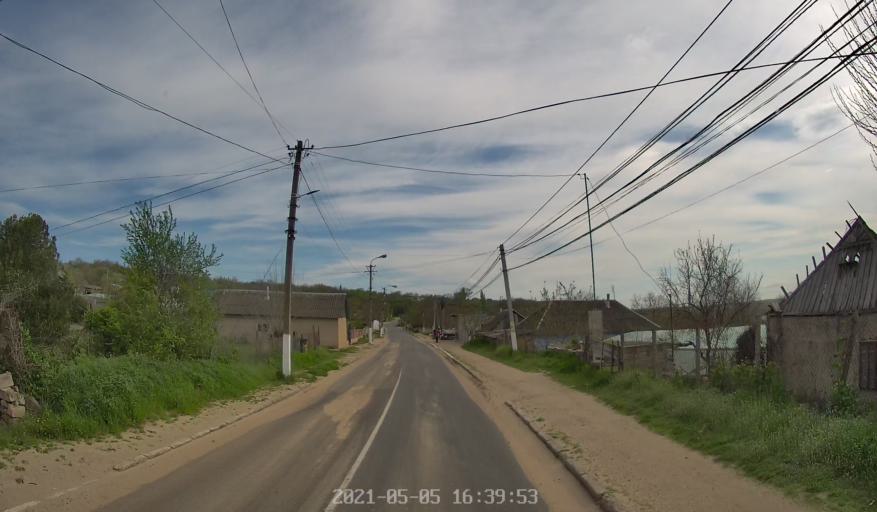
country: MD
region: Criuleni
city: Criuleni
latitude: 47.1239
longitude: 29.1936
